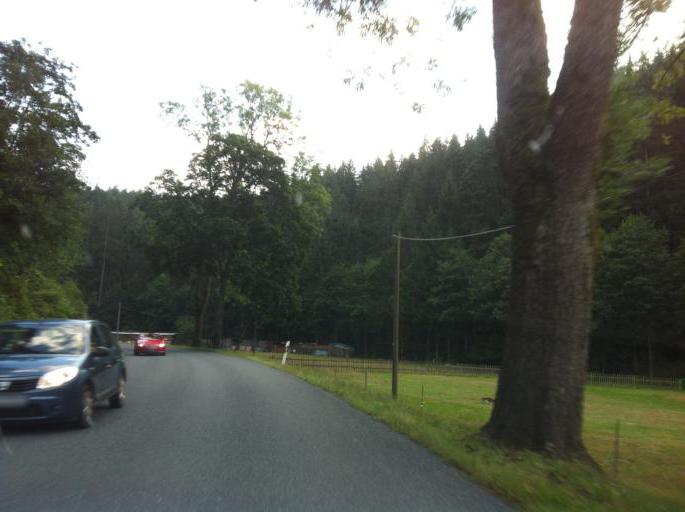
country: DE
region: Thuringia
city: Katzhutte
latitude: 50.5407
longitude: 11.0649
